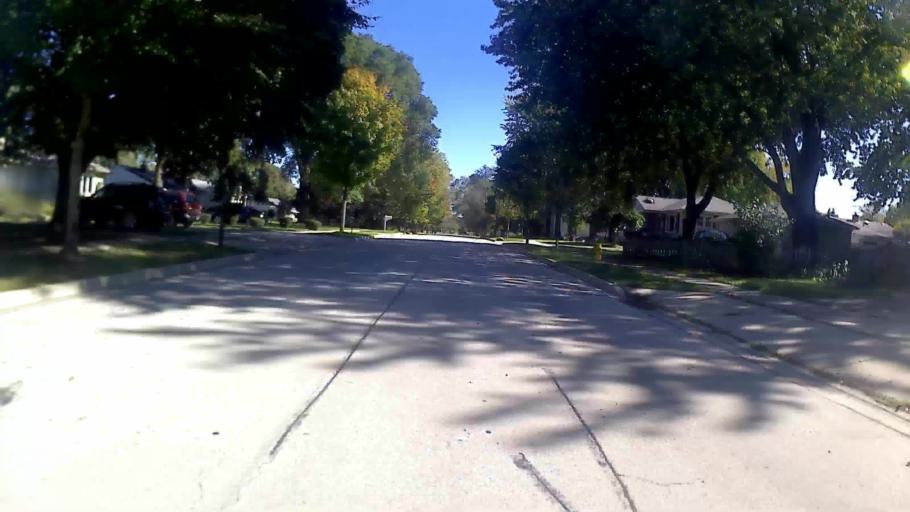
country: US
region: Illinois
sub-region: DuPage County
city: Lombard
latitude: 41.9034
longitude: -88.0105
